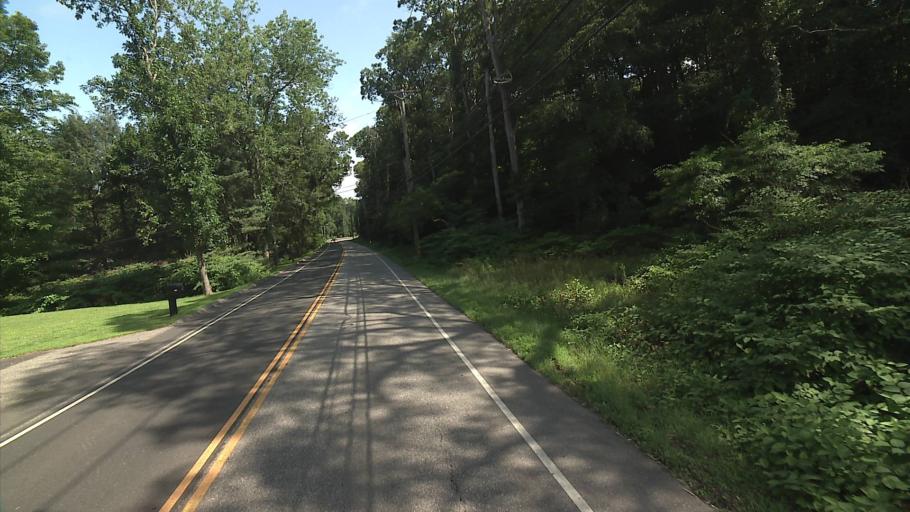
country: US
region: Connecticut
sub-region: Middlesex County
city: Westbrook Center
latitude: 41.3058
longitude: -72.4372
